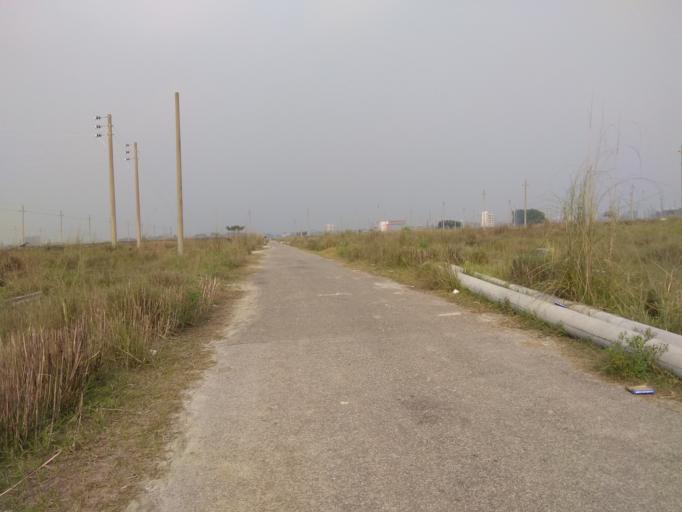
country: BD
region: Dhaka
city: Tungi
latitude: 23.8613
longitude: 90.3697
